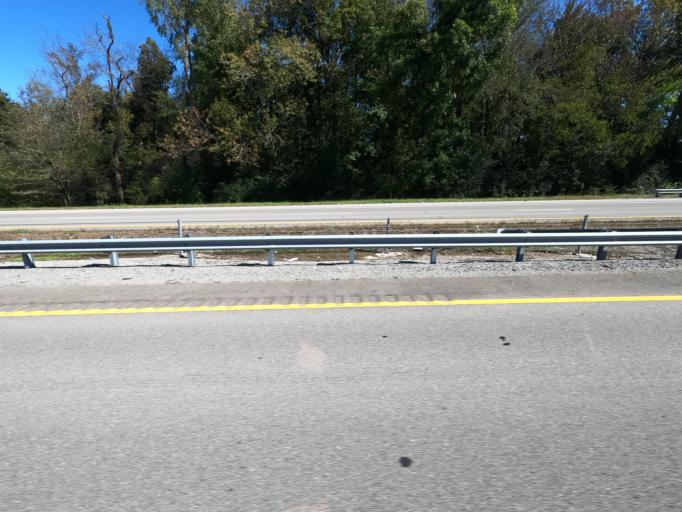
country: US
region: Tennessee
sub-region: Maury County
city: Mount Pleasant
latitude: 35.4078
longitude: -87.2813
